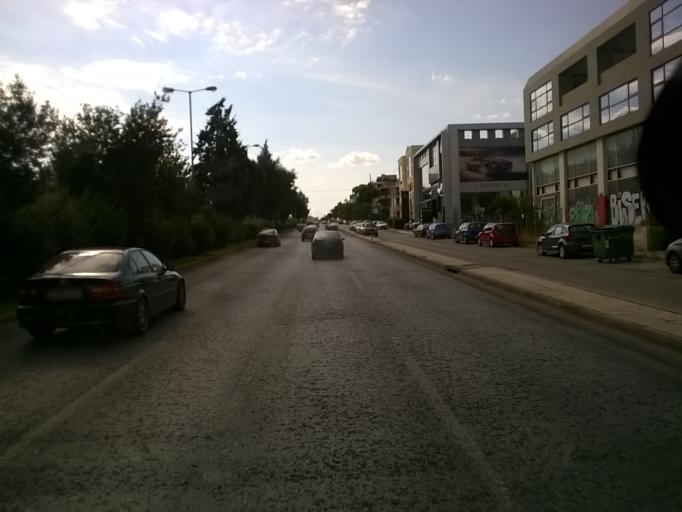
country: GR
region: Attica
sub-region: Nomarchia Athinas
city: Glyfada
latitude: 37.8580
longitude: 23.7647
